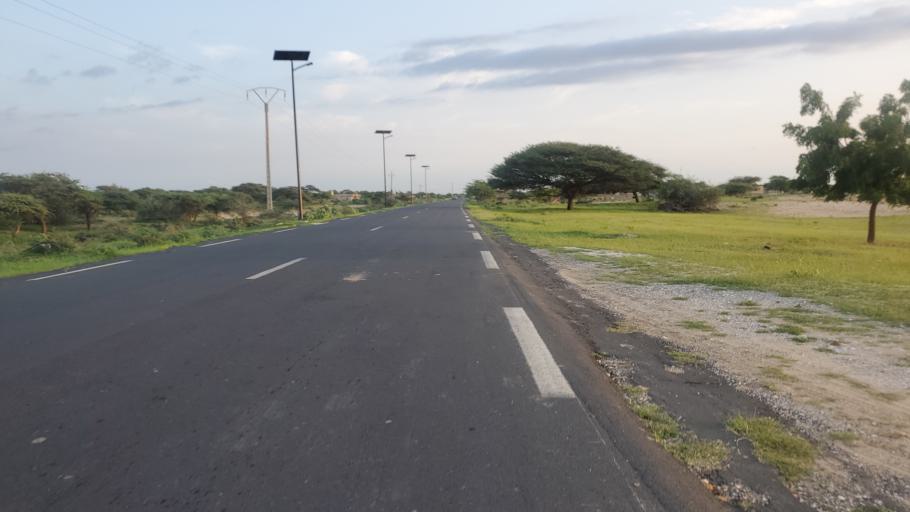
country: SN
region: Saint-Louis
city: Saint-Louis
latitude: 16.1458
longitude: -16.4097
